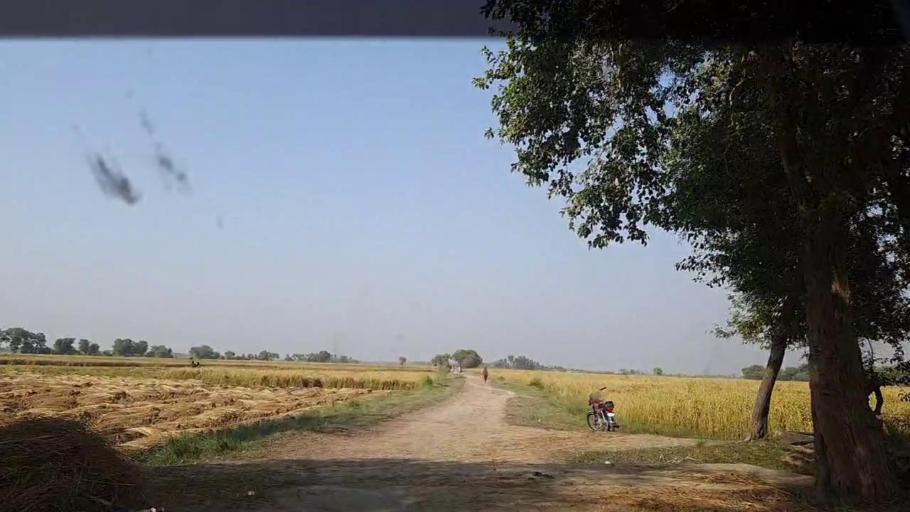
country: PK
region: Sindh
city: Shikarpur
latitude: 28.1233
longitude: 68.5832
